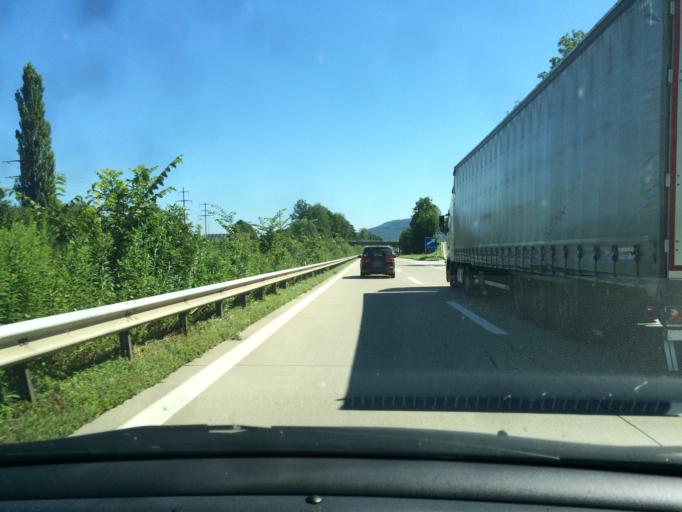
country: CH
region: Saint Gallen
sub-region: Wahlkreis Rheintal
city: Oberriet
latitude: 47.3055
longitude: 9.5654
